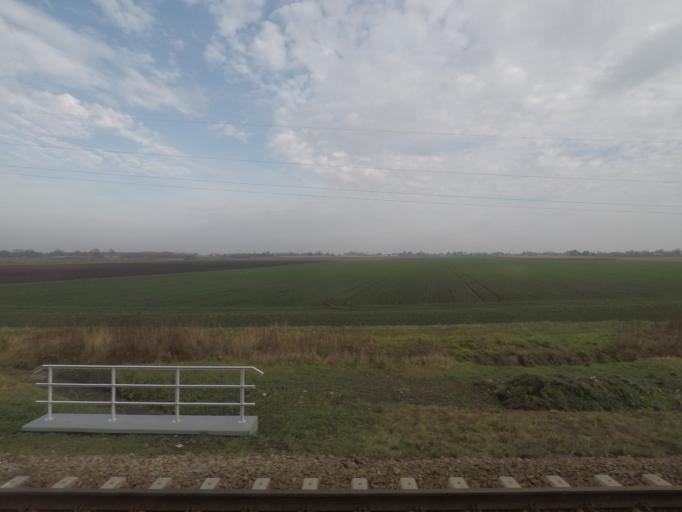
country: PL
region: Subcarpathian Voivodeship
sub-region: Powiat jaroslawski
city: Sosnica
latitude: 49.8850
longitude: 22.8591
